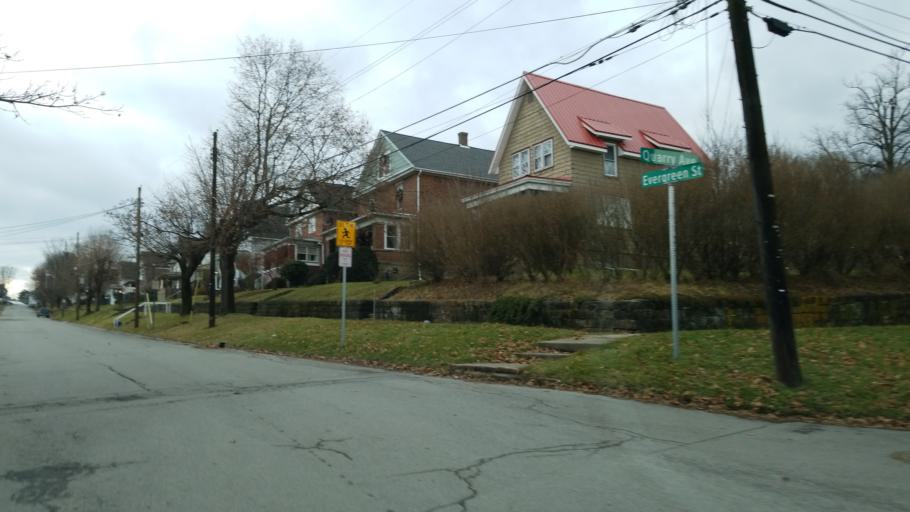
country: US
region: Pennsylvania
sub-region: Clearfield County
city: DuBois
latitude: 41.1247
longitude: -78.7692
